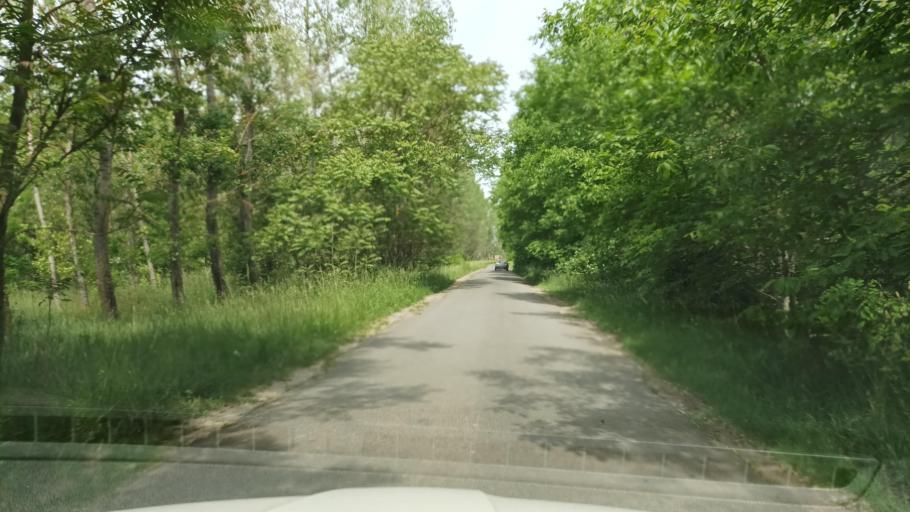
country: HU
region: Fejer
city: Racalmas
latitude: 47.0800
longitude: 18.9392
